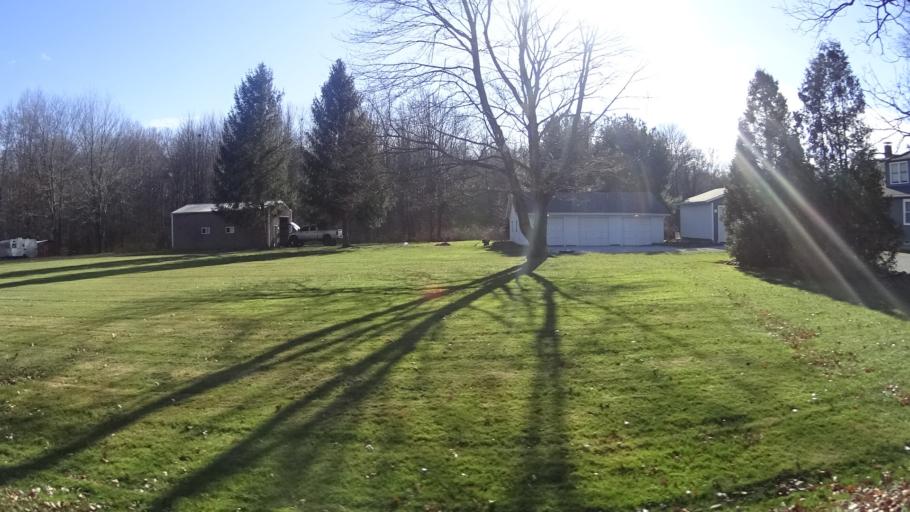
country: US
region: Ohio
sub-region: Lorain County
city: South Amherst
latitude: 41.3142
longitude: -82.2791
